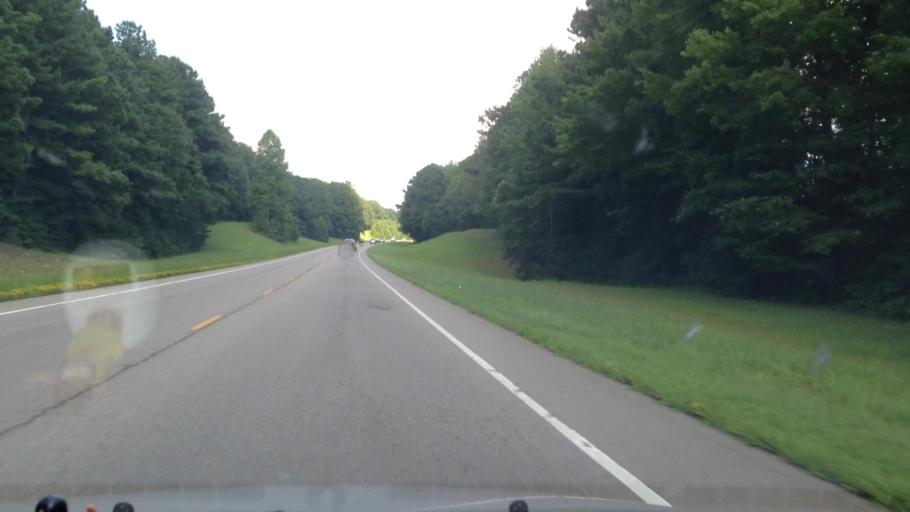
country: US
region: North Carolina
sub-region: Lee County
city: Broadway
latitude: 35.4397
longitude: -79.0794
